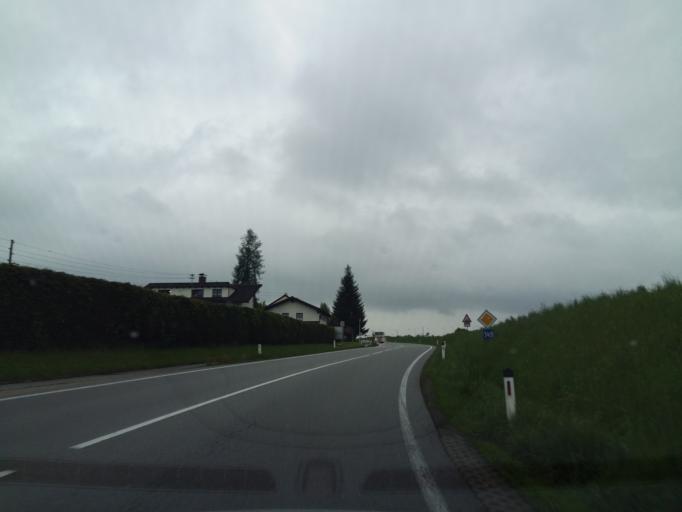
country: AT
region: Upper Austria
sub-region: Politischer Bezirk Scharding
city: Sankt Marienkirchen bei Schaerding
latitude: 48.4052
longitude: 13.4331
